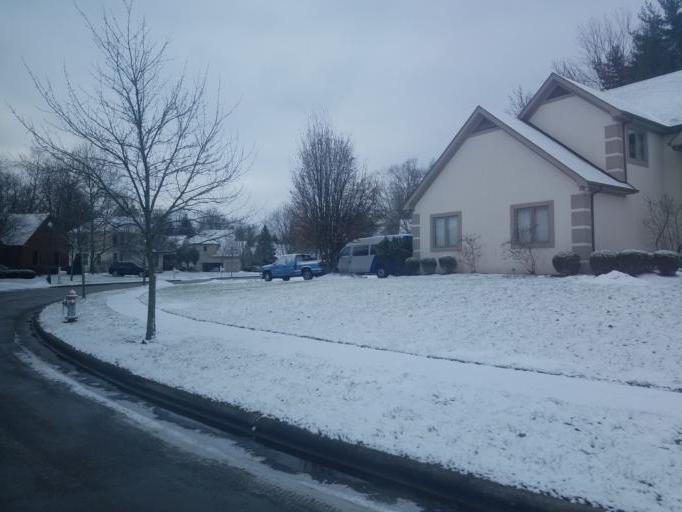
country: US
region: Ohio
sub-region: Franklin County
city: New Albany
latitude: 40.0513
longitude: -82.8340
